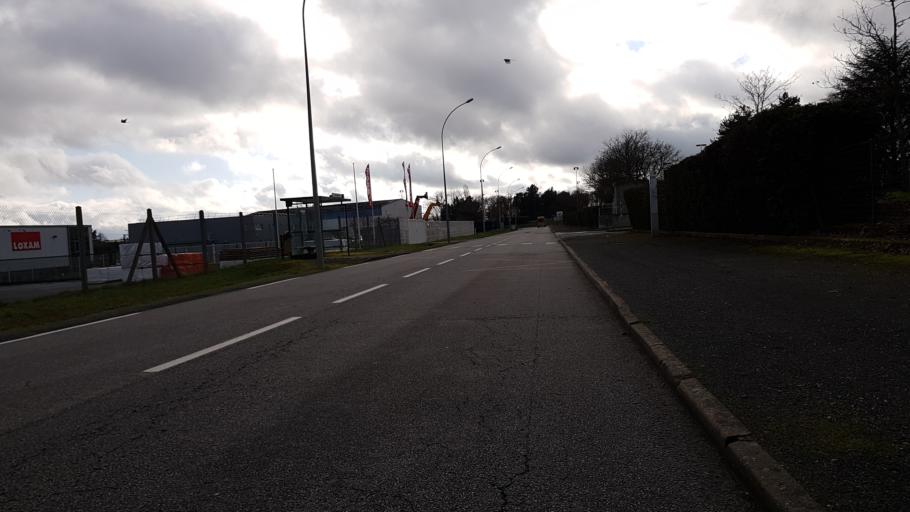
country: FR
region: Poitou-Charentes
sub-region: Departement de la Vienne
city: Chasseneuil-du-Poitou
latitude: 46.6563
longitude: 0.3699
